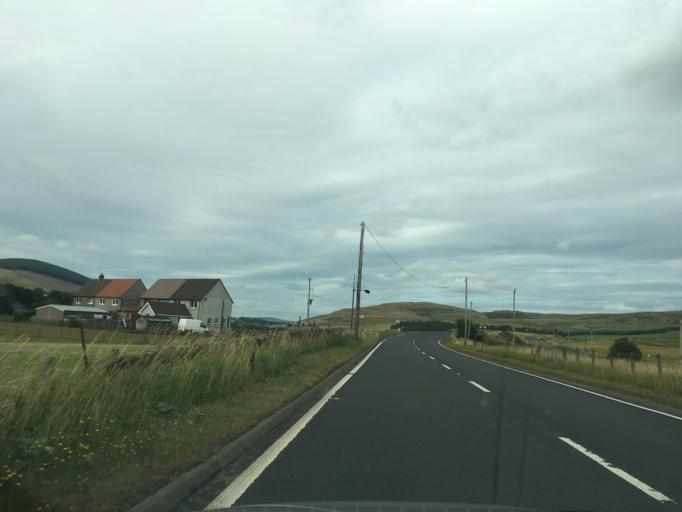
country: GB
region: Scotland
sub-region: South Lanarkshire
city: Douglas
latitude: 55.5214
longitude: -3.6809
